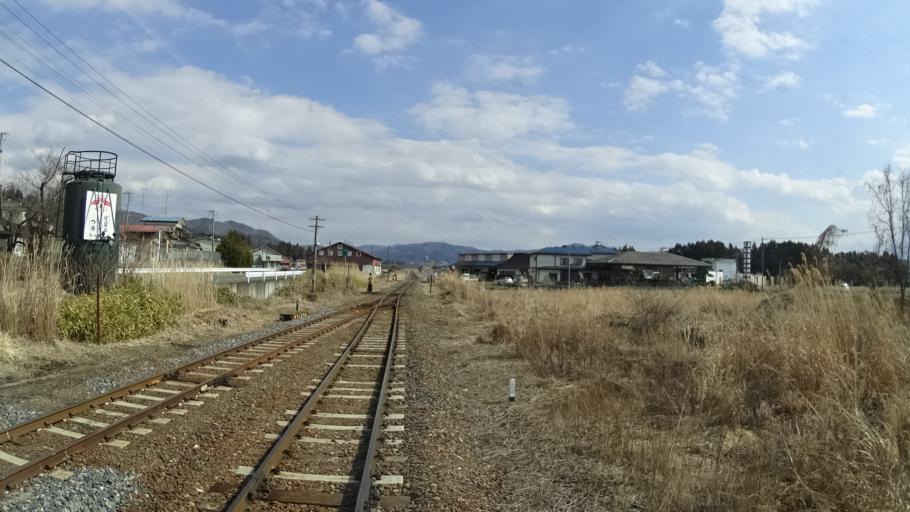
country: JP
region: Iwate
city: Hanamaki
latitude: 39.3826
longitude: 141.2337
